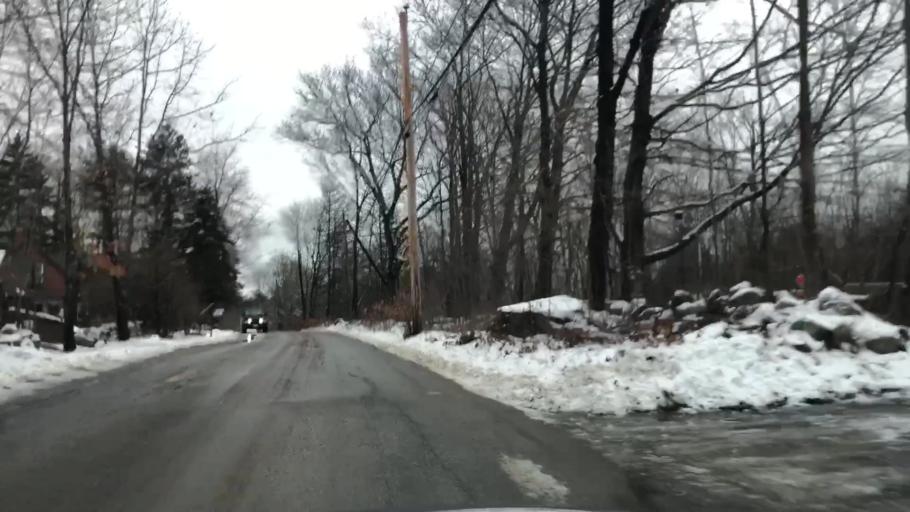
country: US
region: New Hampshire
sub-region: Hillsborough County
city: New Boston
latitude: 43.0128
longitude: -71.6823
